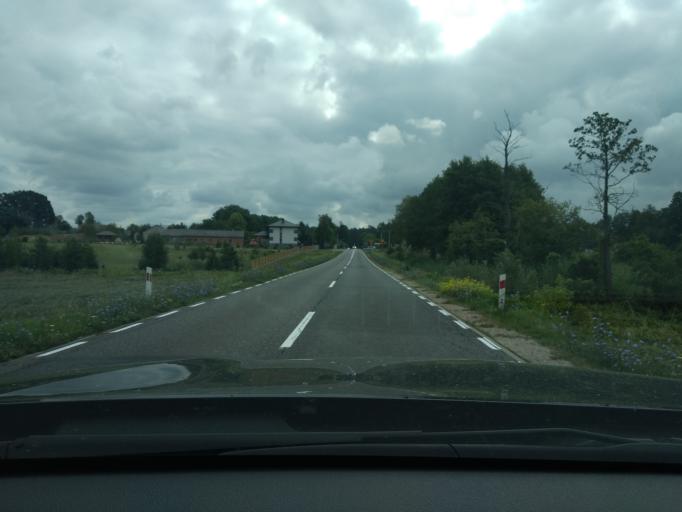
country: PL
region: Masovian Voivodeship
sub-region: Powiat pultuski
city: Obryte
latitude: 52.6485
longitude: 21.2486
